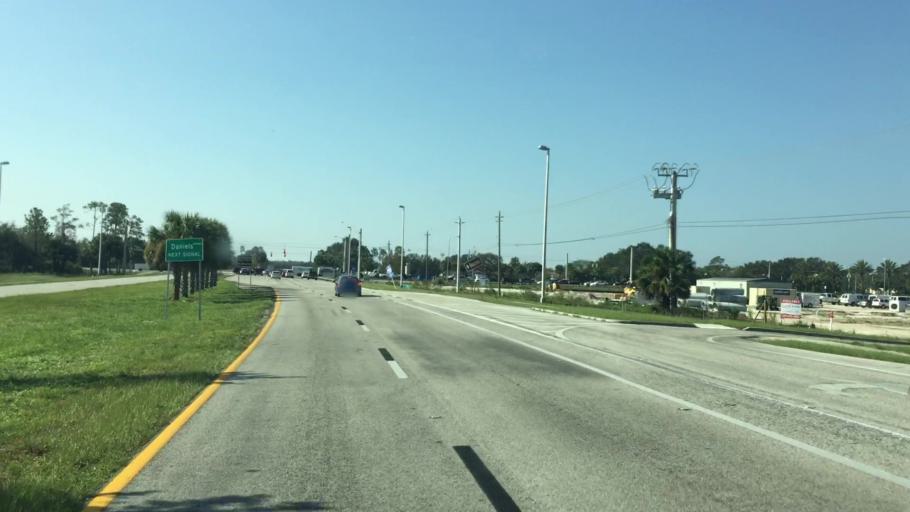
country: US
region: Florida
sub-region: Lee County
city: Villas
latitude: 26.5491
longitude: -81.8393
